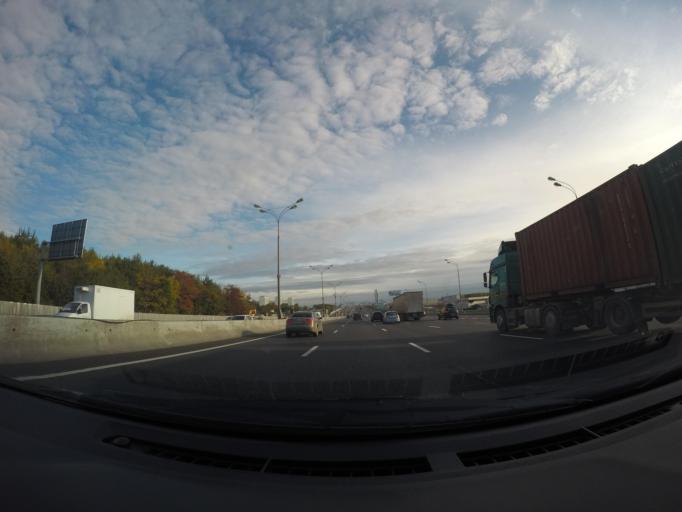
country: RU
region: Moscow
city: Tyoply Stan
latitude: 55.6200
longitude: 37.4815
